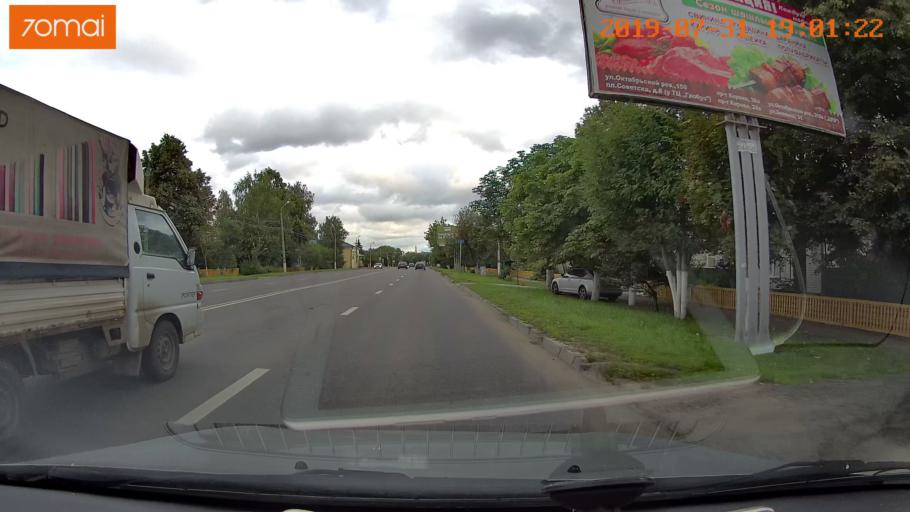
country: RU
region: Moskovskaya
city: Raduzhnyy
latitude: 55.1272
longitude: 38.7287
